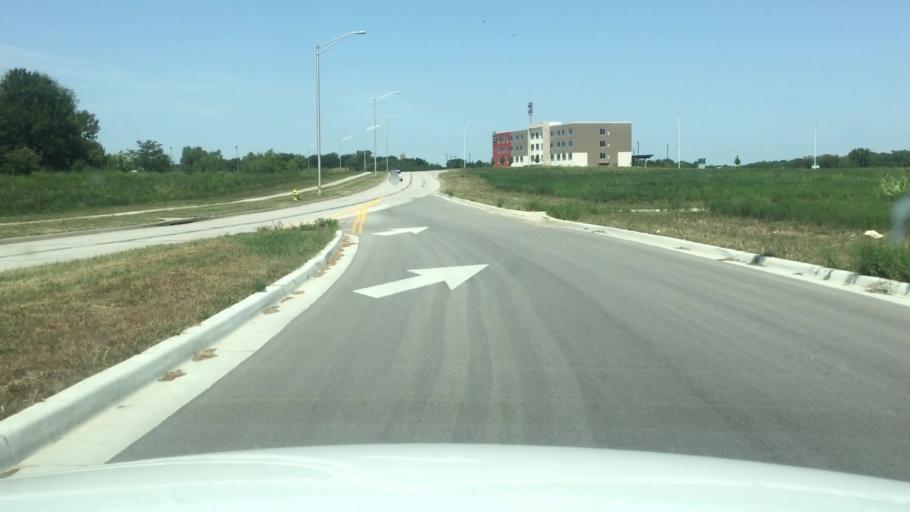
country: US
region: Missouri
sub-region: Jackson County
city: Lees Summit
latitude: 38.9314
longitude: -94.3929
